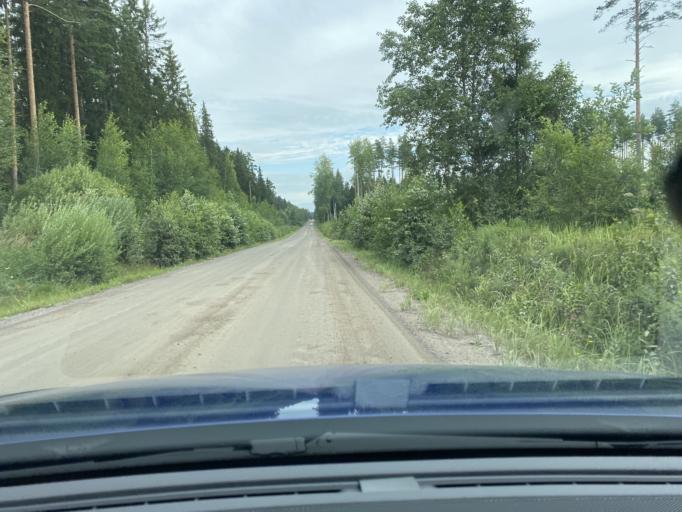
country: FI
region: Satakunta
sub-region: Rauma
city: Kiukainen
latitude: 61.1377
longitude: 21.9917
